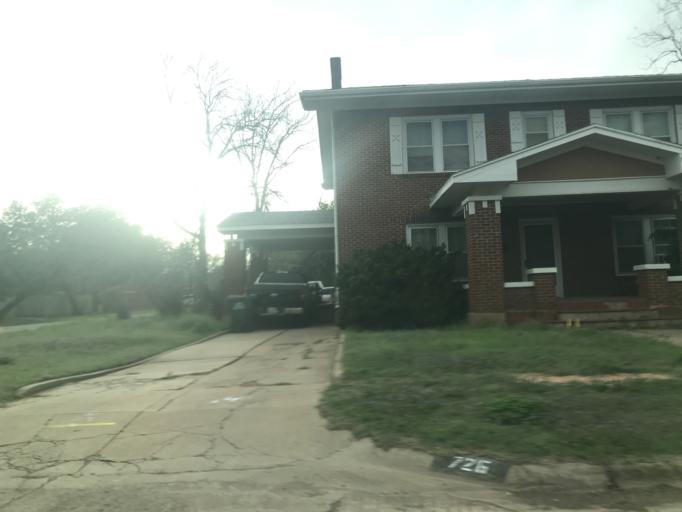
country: US
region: Texas
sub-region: Taylor County
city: Abilene
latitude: 32.4428
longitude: -99.7657
